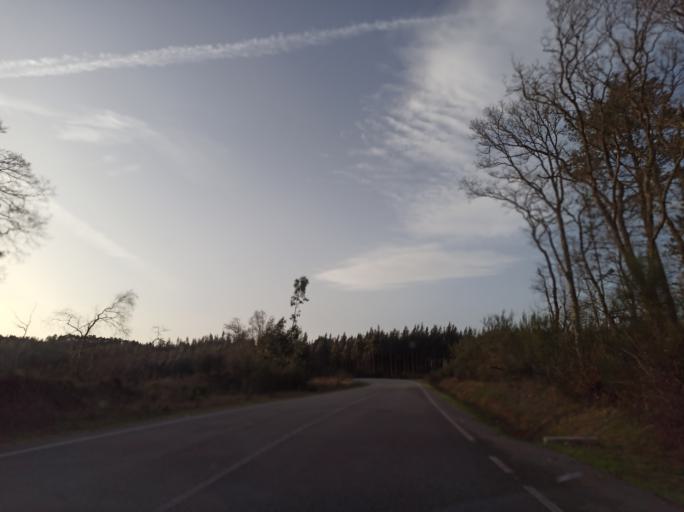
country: ES
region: Galicia
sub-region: Provincia de Lugo
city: Friol
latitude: 43.0252
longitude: -7.8742
